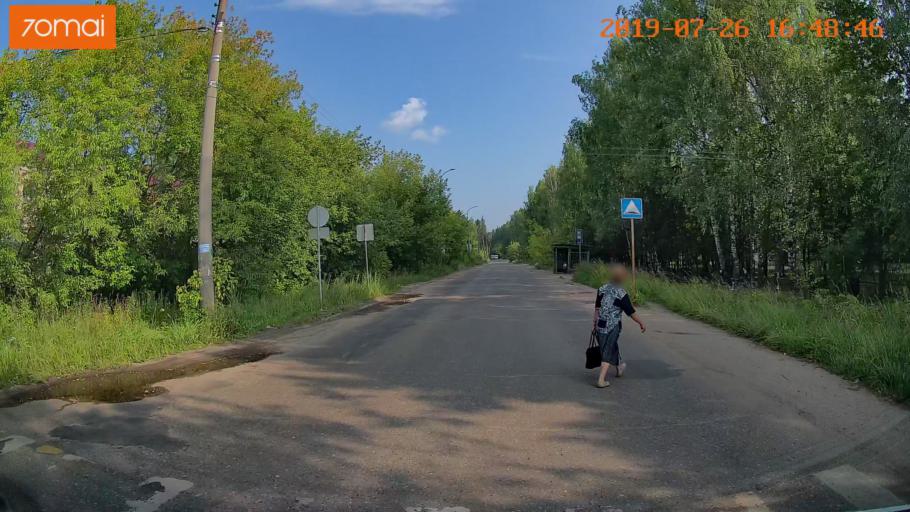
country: RU
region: Ivanovo
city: Bogorodskoye
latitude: 57.0330
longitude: 41.0170
